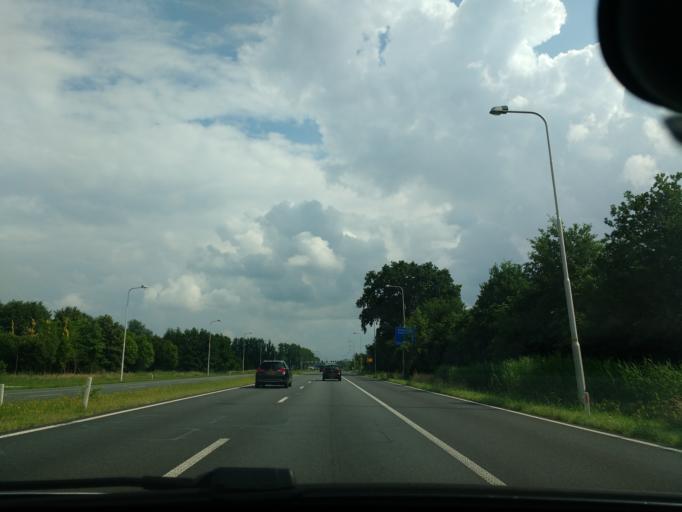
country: NL
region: Gelderland
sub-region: Gemeente Ede
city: Bennekom
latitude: 52.0059
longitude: 5.6545
